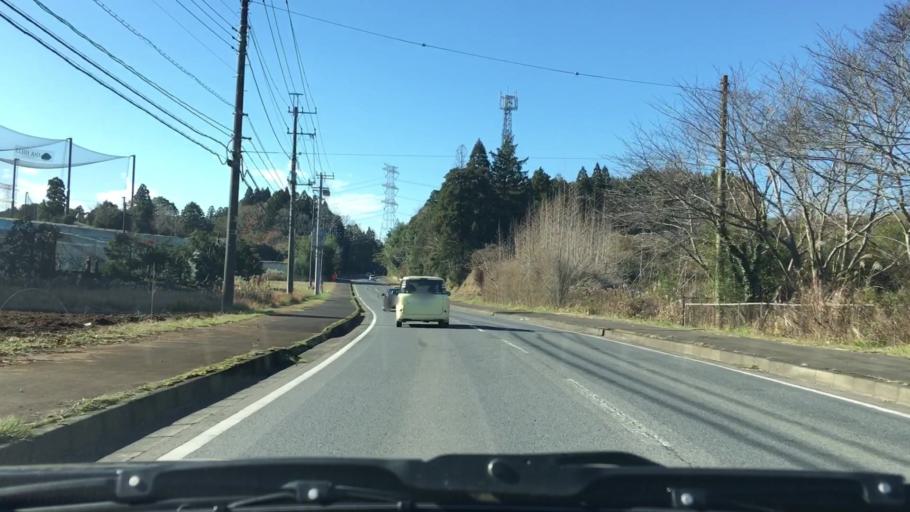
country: JP
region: Chiba
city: Sawara
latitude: 35.8098
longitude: 140.4903
